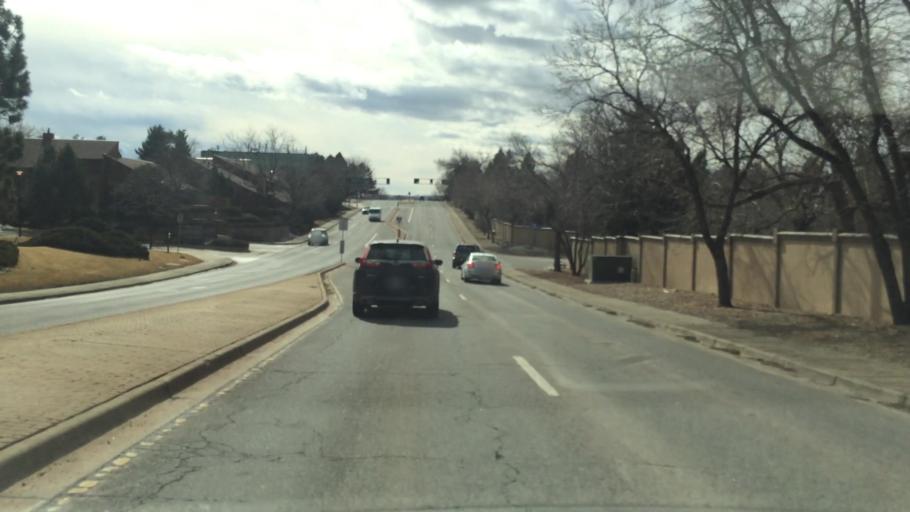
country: US
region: Colorado
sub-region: Arapahoe County
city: Castlewood
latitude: 39.6006
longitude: -104.9042
